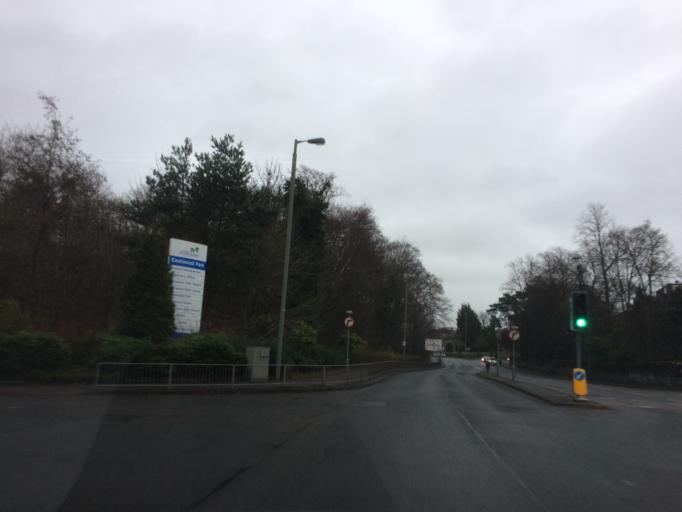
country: GB
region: Scotland
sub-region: East Renfrewshire
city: Giffnock
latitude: 55.7969
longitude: -4.3048
